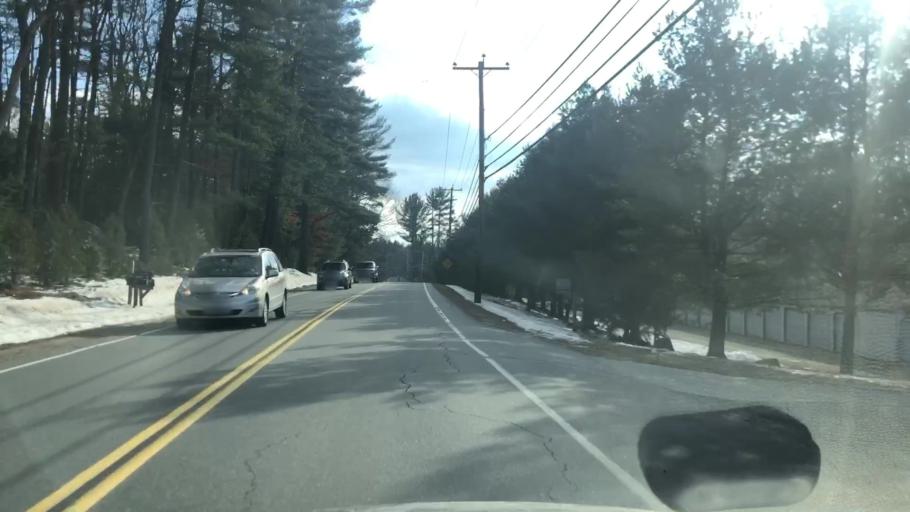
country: US
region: New Hampshire
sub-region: Hillsborough County
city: Milford
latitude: 42.8499
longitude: -71.6625
